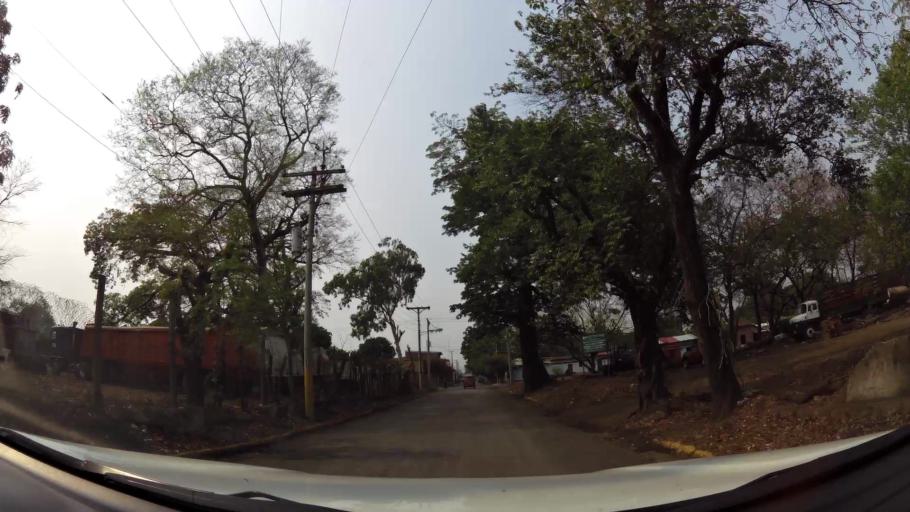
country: NI
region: Chinandega
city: Chinandega
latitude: 12.6232
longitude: -87.1326
